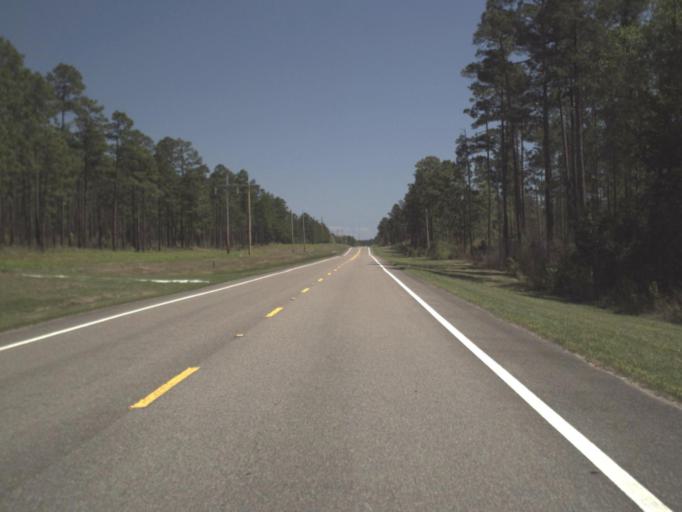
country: US
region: Florida
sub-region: Santa Rosa County
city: Point Baker
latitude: 30.8697
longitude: -86.9266
